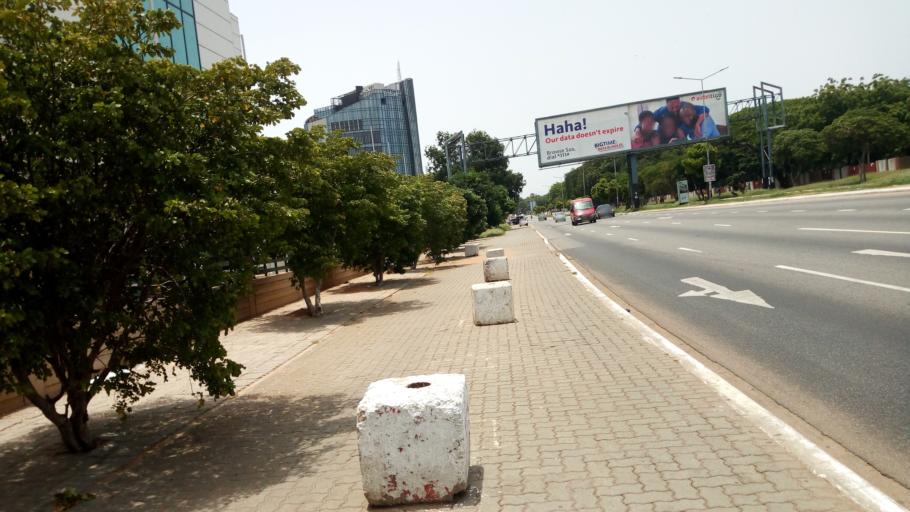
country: GH
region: Greater Accra
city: Accra
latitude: 5.5557
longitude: -0.2003
